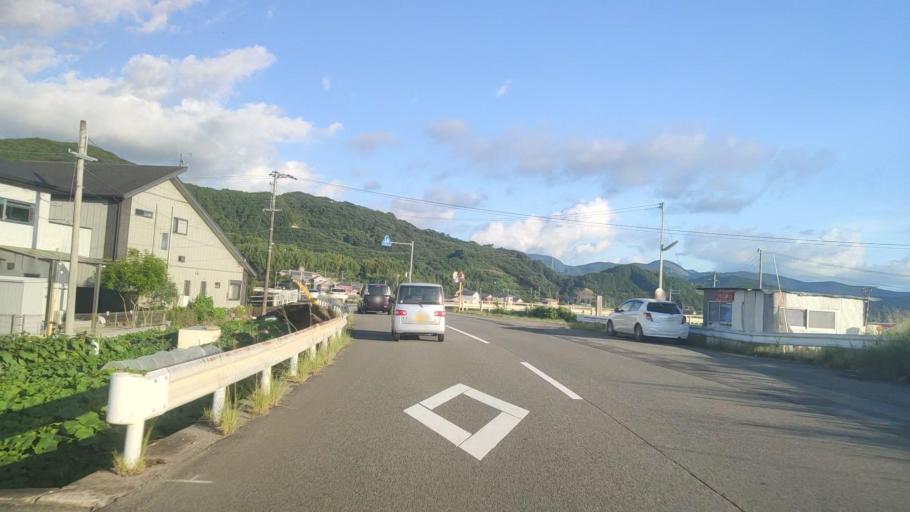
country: JP
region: Wakayama
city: Tanabe
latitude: 33.7183
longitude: 135.4462
